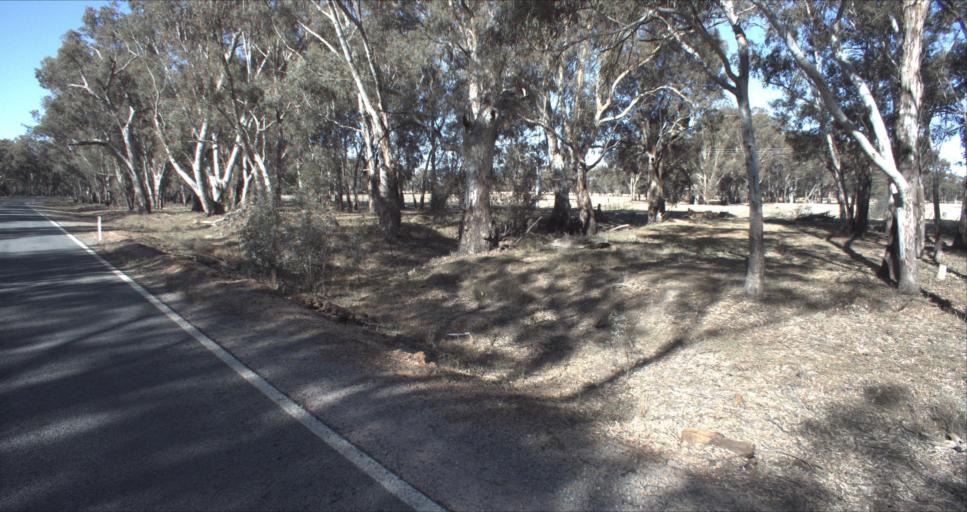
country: AU
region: New South Wales
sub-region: Leeton
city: Leeton
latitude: -34.6266
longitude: 146.3789
